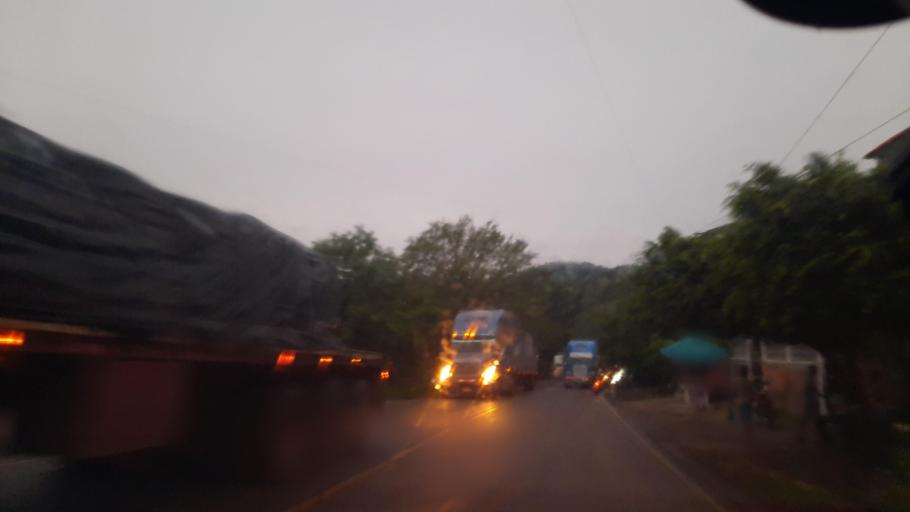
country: GT
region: Jutiapa
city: Atescatempa
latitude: 14.2040
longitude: -89.6807
